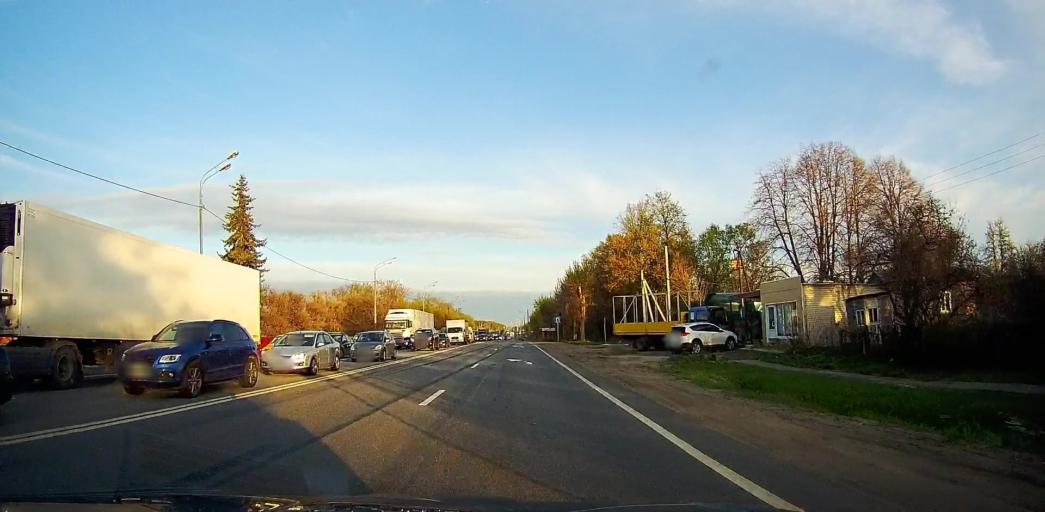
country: RU
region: Moskovskaya
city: Troitskoye
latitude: 55.2423
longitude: 38.5364
